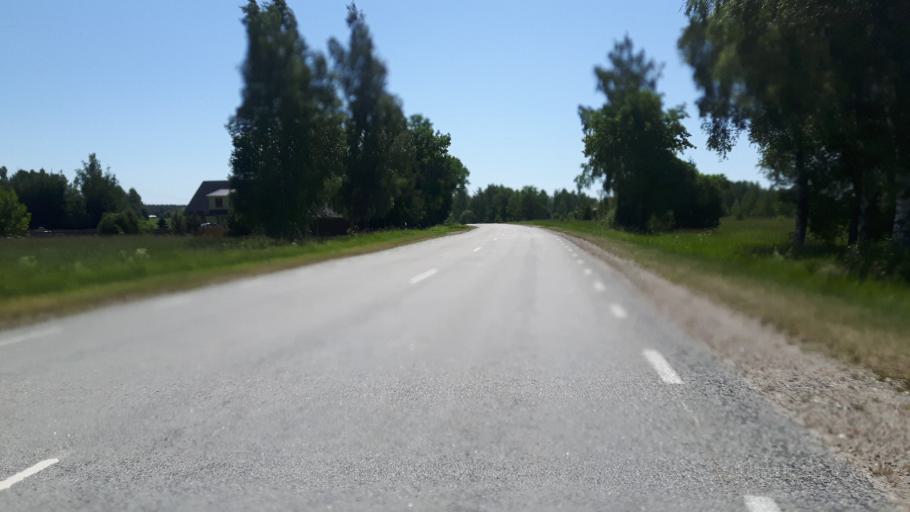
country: EE
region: Paernumaa
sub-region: Sindi linn
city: Sindi
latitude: 58.4338
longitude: 24.7327
